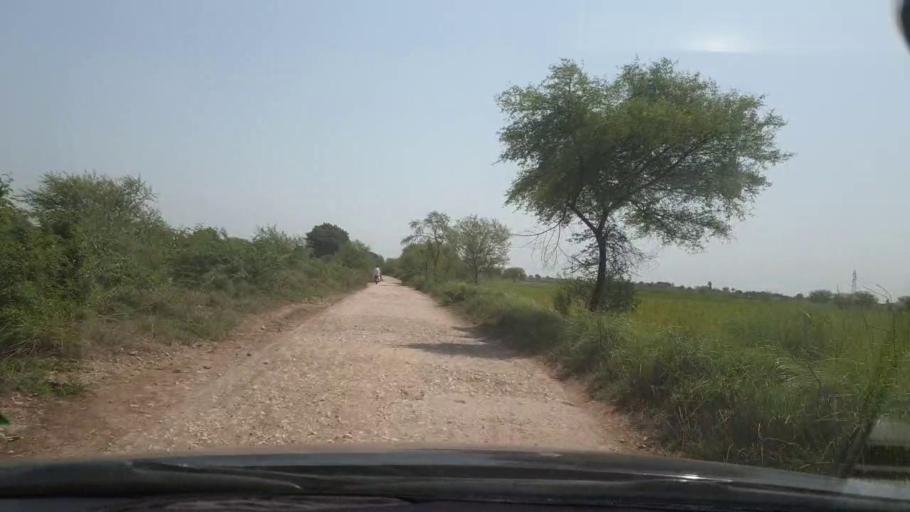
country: PK
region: Sindh
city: Tando Bago
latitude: 24.7722
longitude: 69.1910
